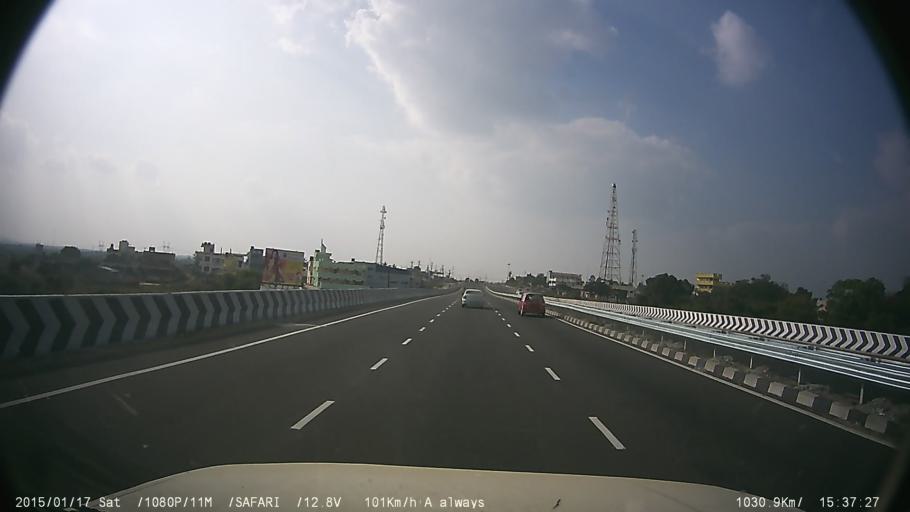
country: IN
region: Tamil Nadu
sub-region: Krishnagiri
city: Kelamangalam
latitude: 12.6633
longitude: 78.0082
